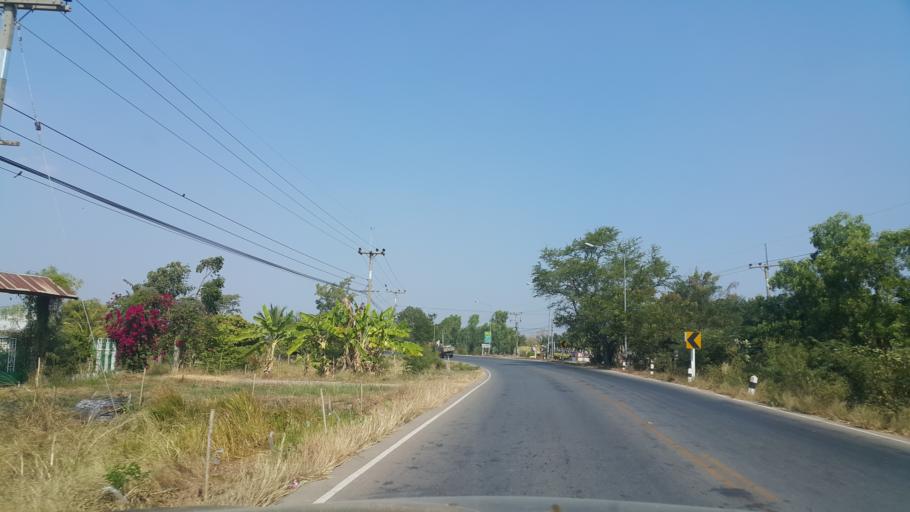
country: TH
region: Chaiyaphum
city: Khon Sawan
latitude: 15.8932
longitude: 102.2561
